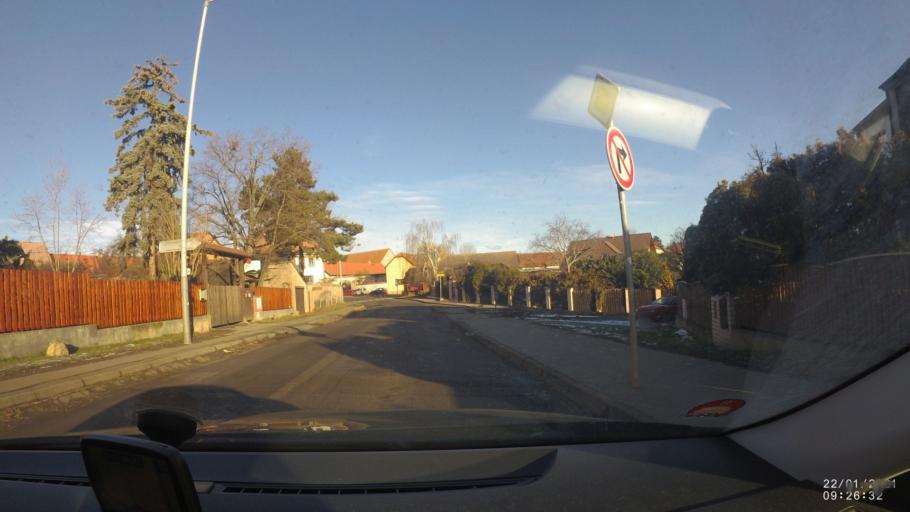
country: CZ
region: Praha
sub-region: Praha 12
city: Modrany
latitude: 50.0180
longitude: 14.3569
